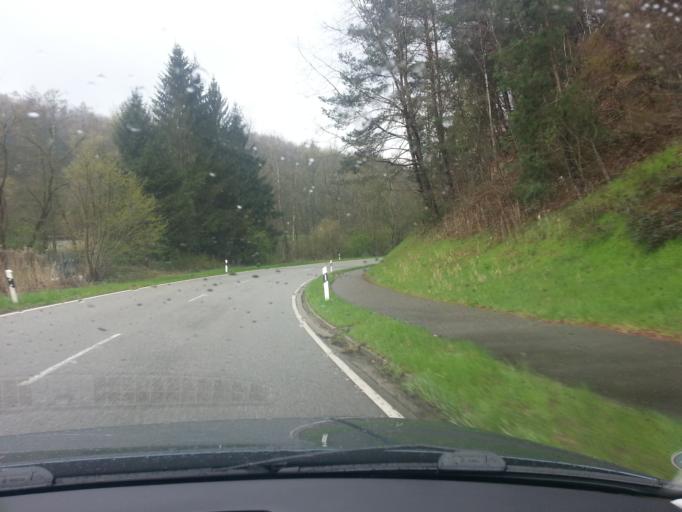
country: DE
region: Rheinland-Pfalz
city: Donsieders
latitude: 49.2530
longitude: 7.6060
